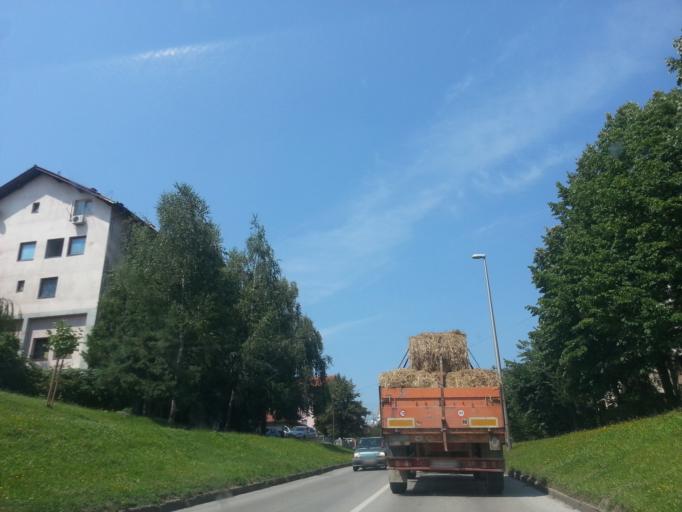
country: BA
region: Brcko
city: Brcko
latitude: 44.8662
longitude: 18.8110
